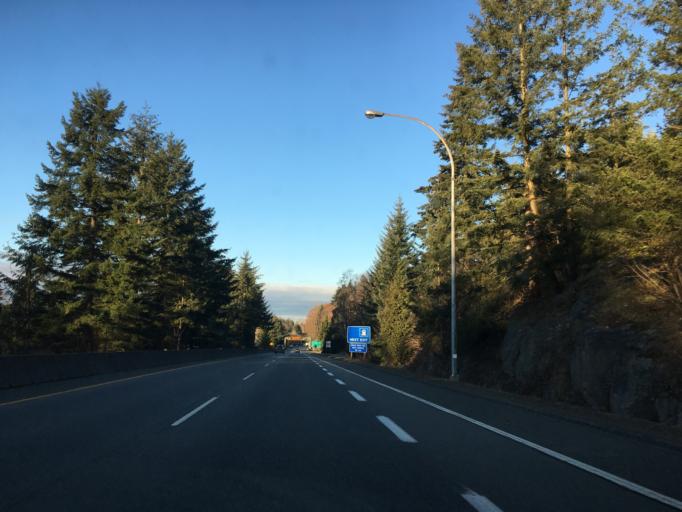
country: CA
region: British Columbia
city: West Vancouver
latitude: 49.3470
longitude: -123.2023
